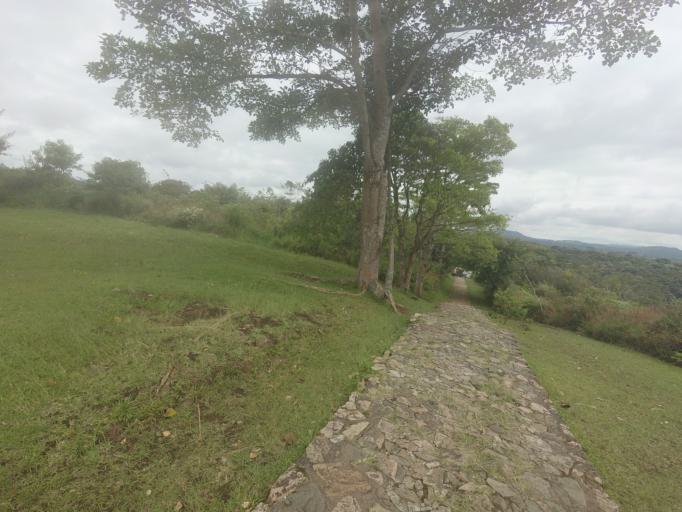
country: CO
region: Huila
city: San Agustin
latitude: 1.8807
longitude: -76.3029
